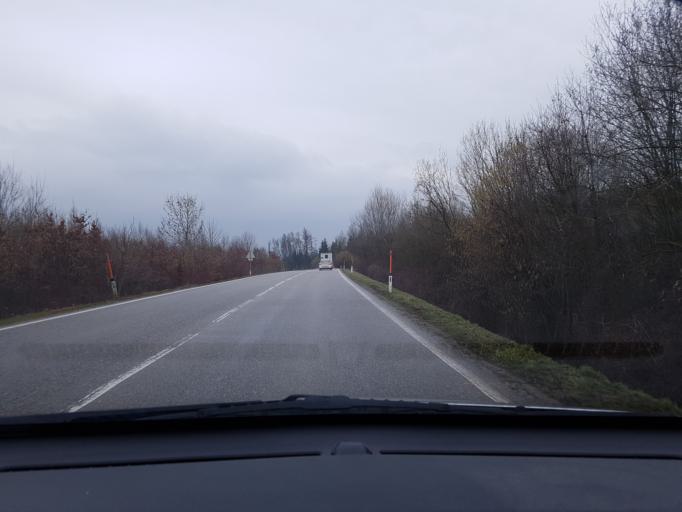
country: AT
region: Upper Austria
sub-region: Steyr Stadt
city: Steyr
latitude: 48.0608
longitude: 14.3879
